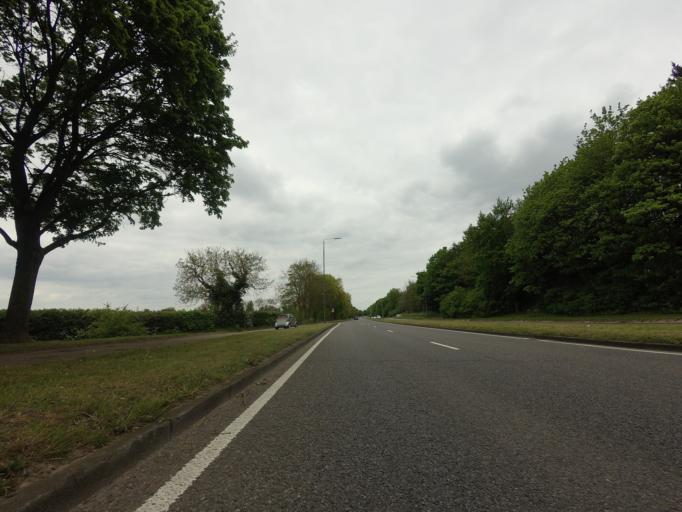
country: GB
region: England
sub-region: Greater London
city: Bexley
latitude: 51.4319
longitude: 0.1416
